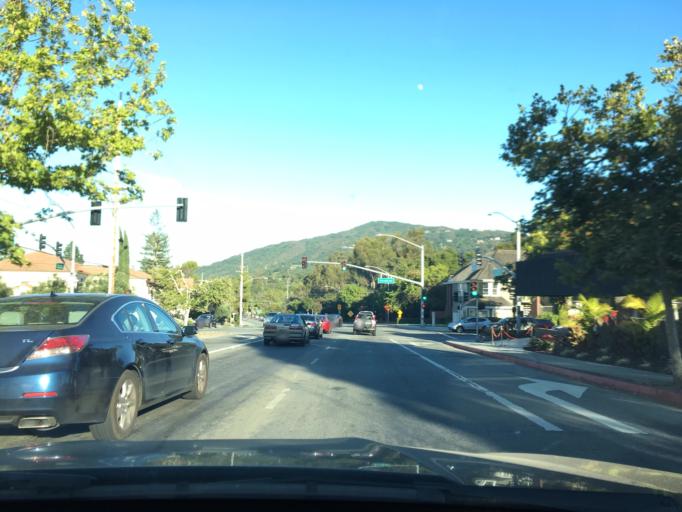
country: US
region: California
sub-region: Santa Clara County
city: Los Gatos
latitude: 37.2284
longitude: -121.9801
